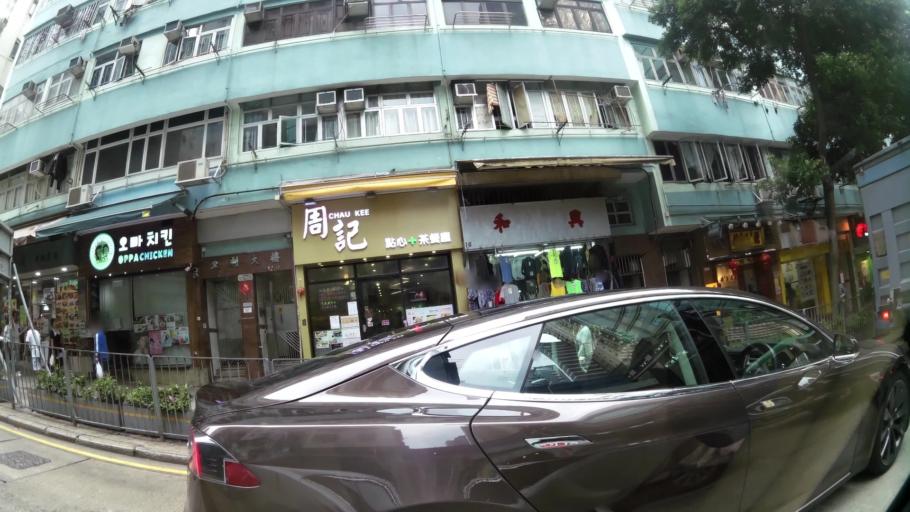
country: HK
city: Hong Kong
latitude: 22.2868
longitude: 114.1385
